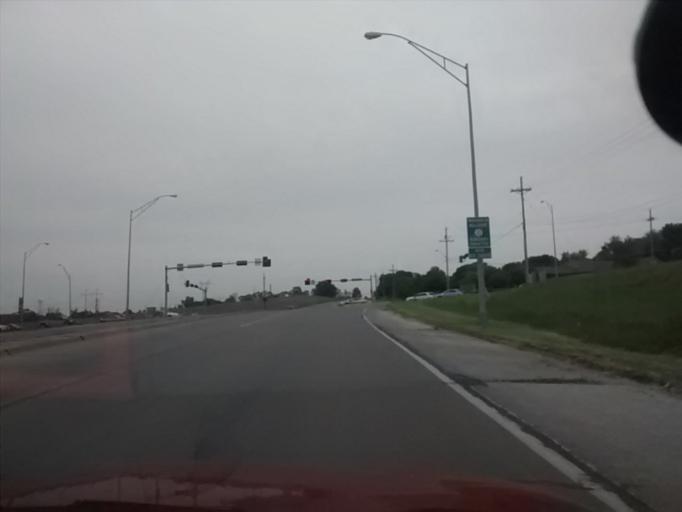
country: US
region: Nebraska
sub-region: Sarpy County
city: Offutt Air Force Base
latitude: 41.1608
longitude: -95.9669
